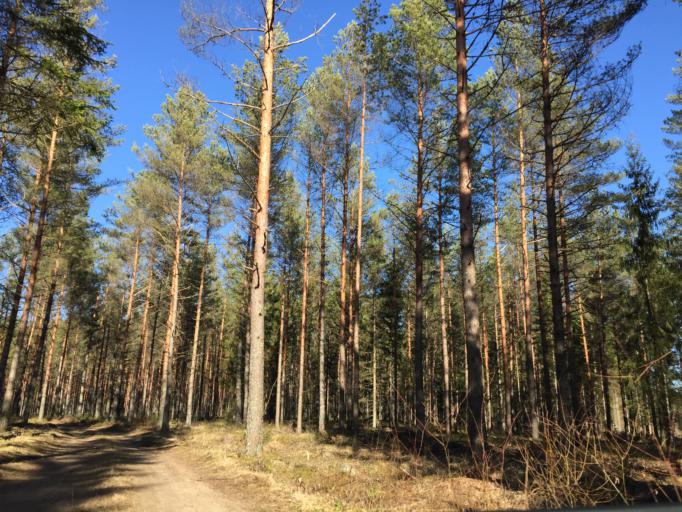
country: LV
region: Ropazu
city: Ropazi
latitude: 56.8883
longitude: 24.7102
